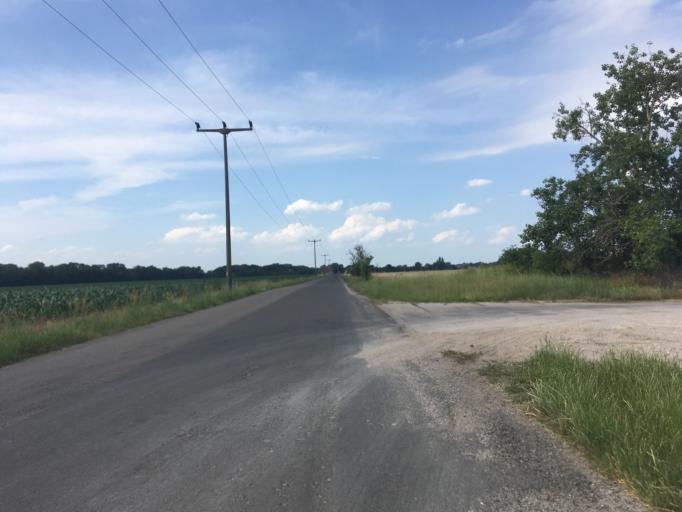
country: DE
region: Saxony-Anhalt
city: Quellendorf
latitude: 51.7746
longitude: 12.0929
